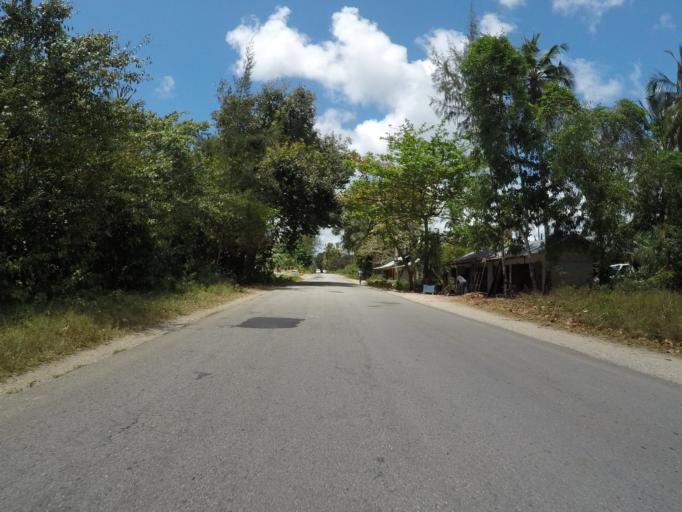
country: TZ
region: Zanzibar Central/South
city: Nganane
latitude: -6.2853
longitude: 39.4365
